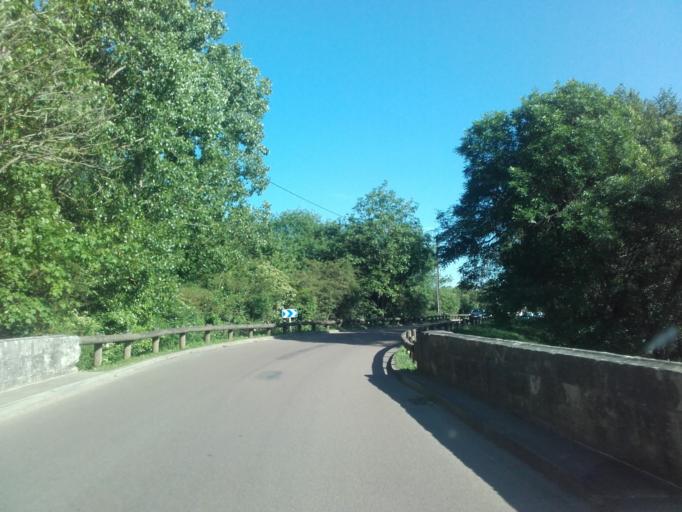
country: FR
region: Bourgogne
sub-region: Departement de Saone-et-Loire
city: Demigny
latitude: 46.9349
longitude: 4.8323
